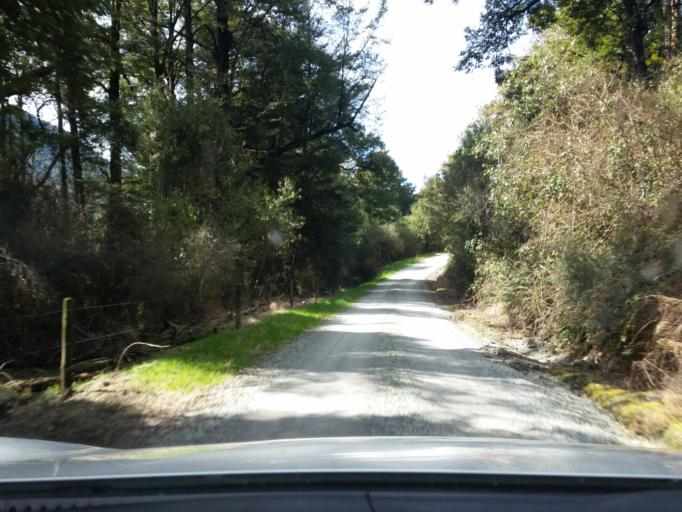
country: NZ
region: West Coast
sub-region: Buller District
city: Westport
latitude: -42.0026
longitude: 172.3366
